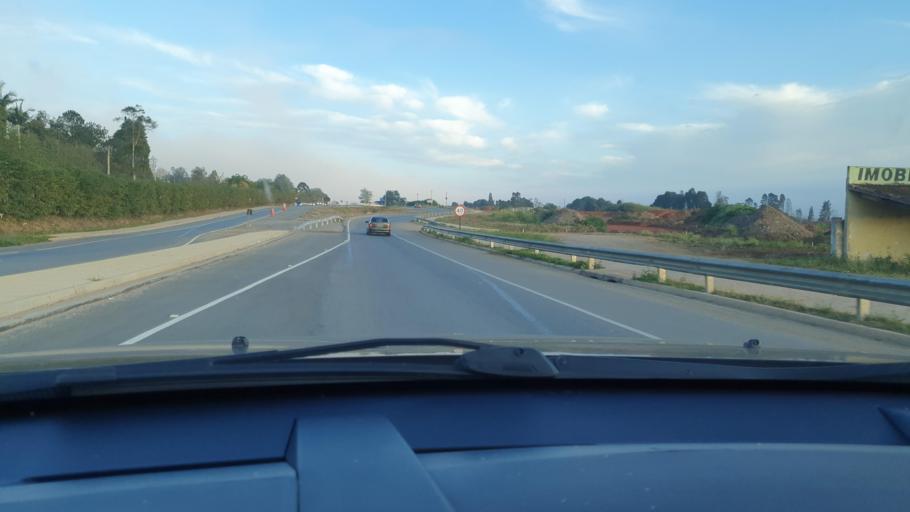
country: BR
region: Sao Paulo
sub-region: Ibiuna
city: Ibiuna
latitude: -23.6487
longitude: -47.1378
